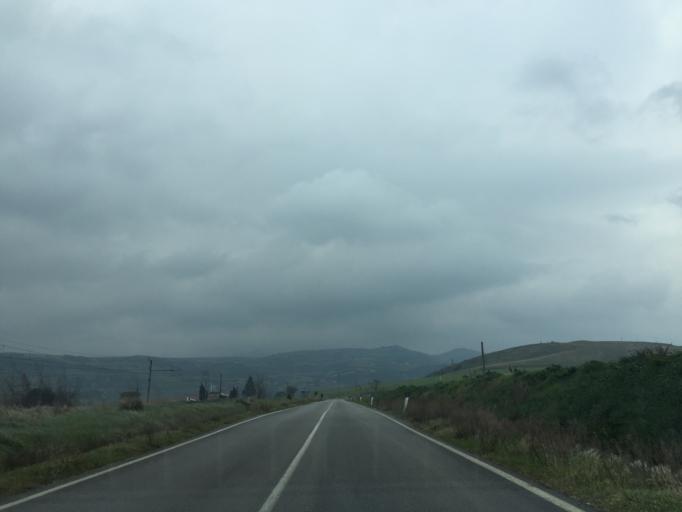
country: IT
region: Apulia
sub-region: Provincia di Foggia
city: Bovino
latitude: 41.2886
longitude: 15.3802
